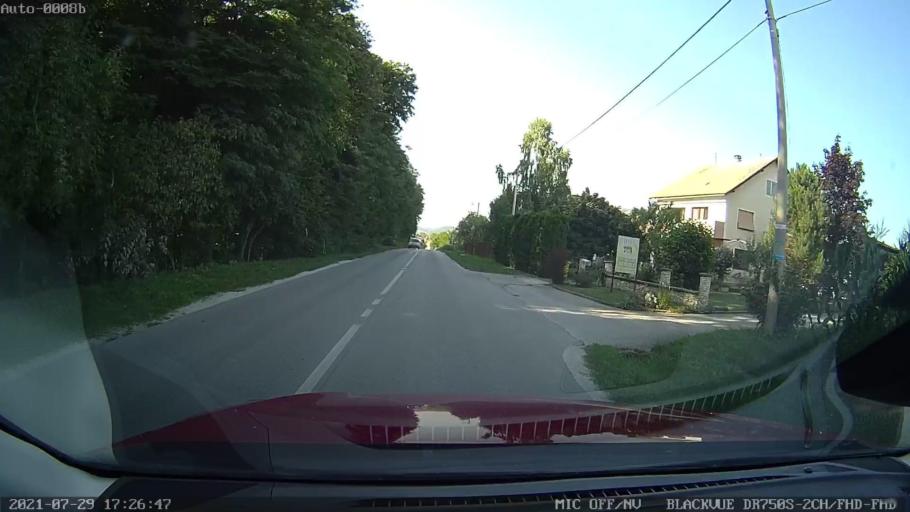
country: HR
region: Varazdinska
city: Ivanec
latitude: 46.2562
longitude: 16.1174
